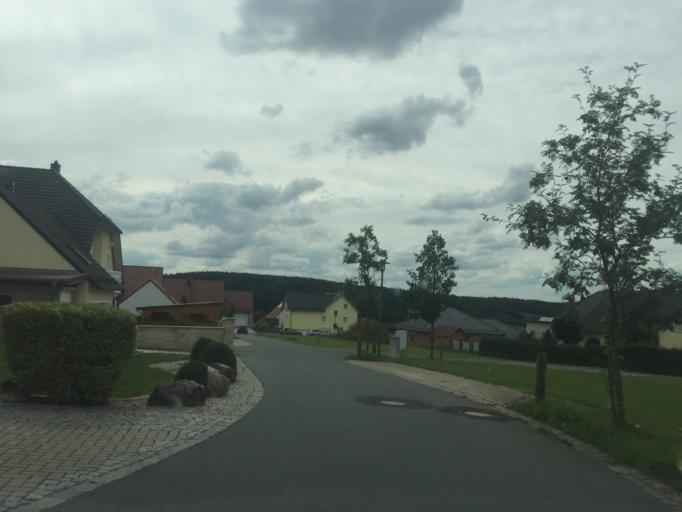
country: DE
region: Bavaria
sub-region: Upper Palatinate
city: Pressath
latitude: 49.7741
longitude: 11.9341
